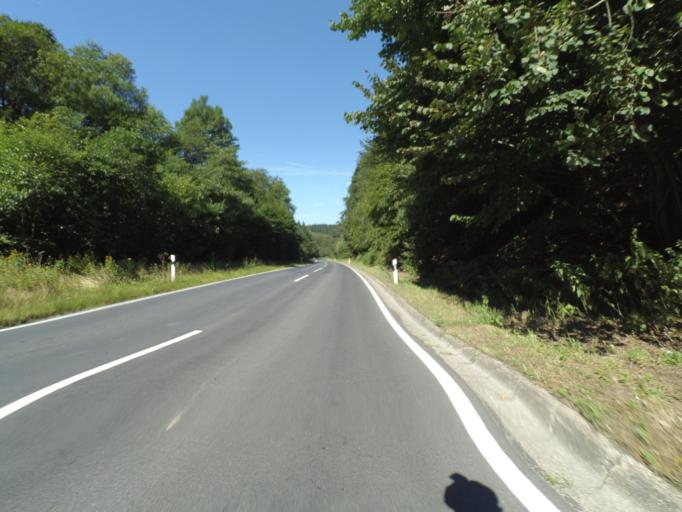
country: DE
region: Rheinland-Pfalz
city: Mullenbach
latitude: 50.1939
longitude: 7.0615
